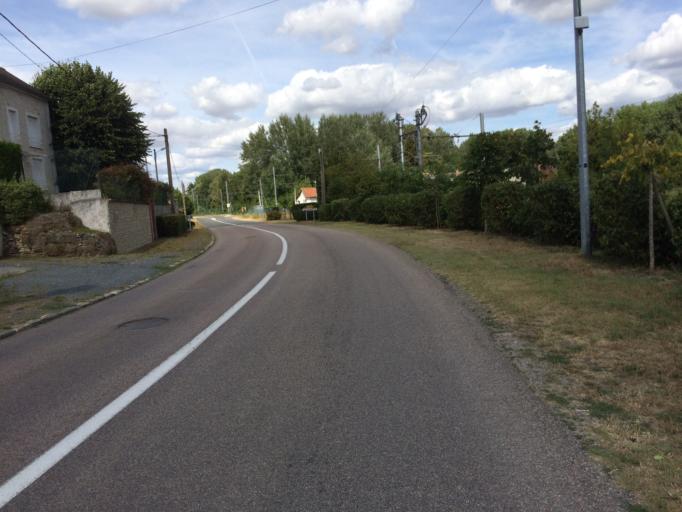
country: FR
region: Ile-de-France
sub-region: Departement de l'Essonne
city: Maisse
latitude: 48.3433
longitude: 2.3791
